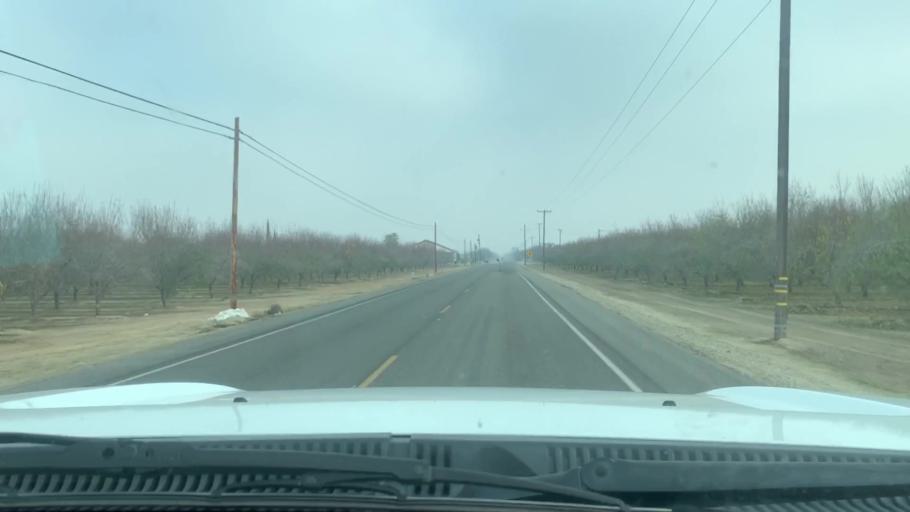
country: US
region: California
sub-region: Kern County
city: Shafter
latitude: 35.4999
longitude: -119.2993
